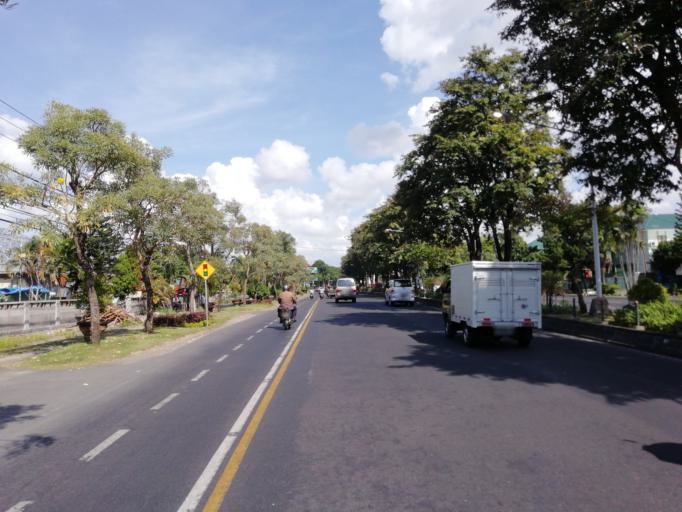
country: ID
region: Bali
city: Denpasar
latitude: -8.6699
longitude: 115.2203
